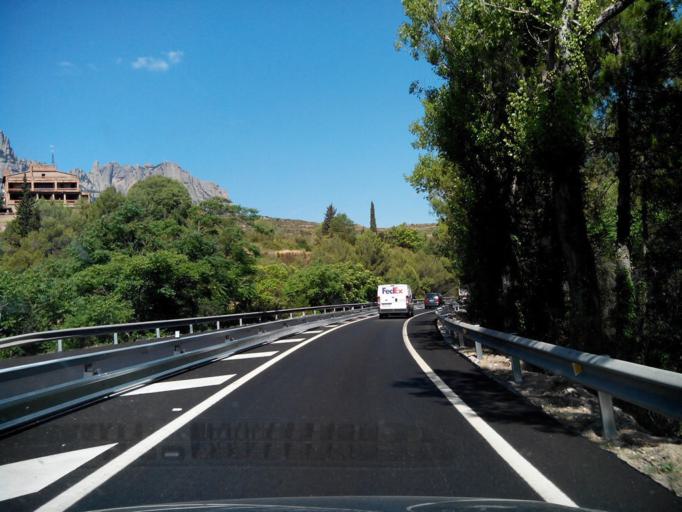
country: ES
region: Catalonia
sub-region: Provincia de Barcelona
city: Monistrol de Montserrat
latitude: 41.6022
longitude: 1.8746
